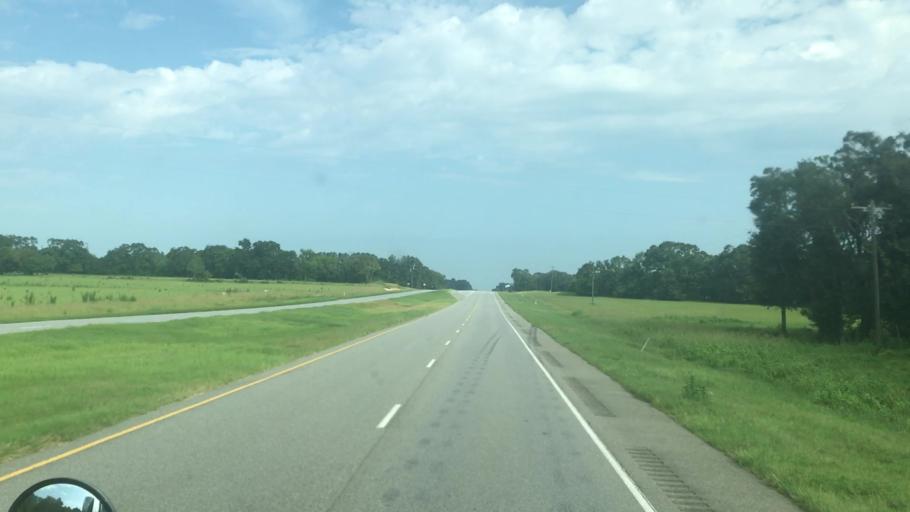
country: US
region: Georgia
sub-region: Early County
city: Blakely
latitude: 31.3064
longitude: -84.8664
